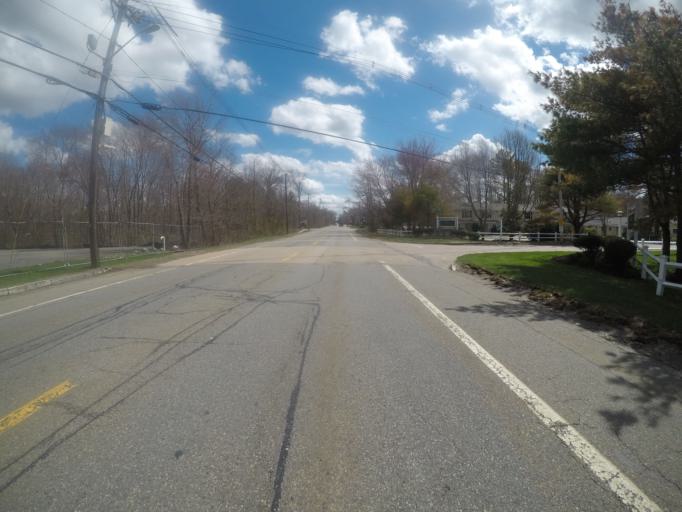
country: US
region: Massachusetts
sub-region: Bristol County
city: Easton
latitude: 42.0366
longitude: -71.0744
